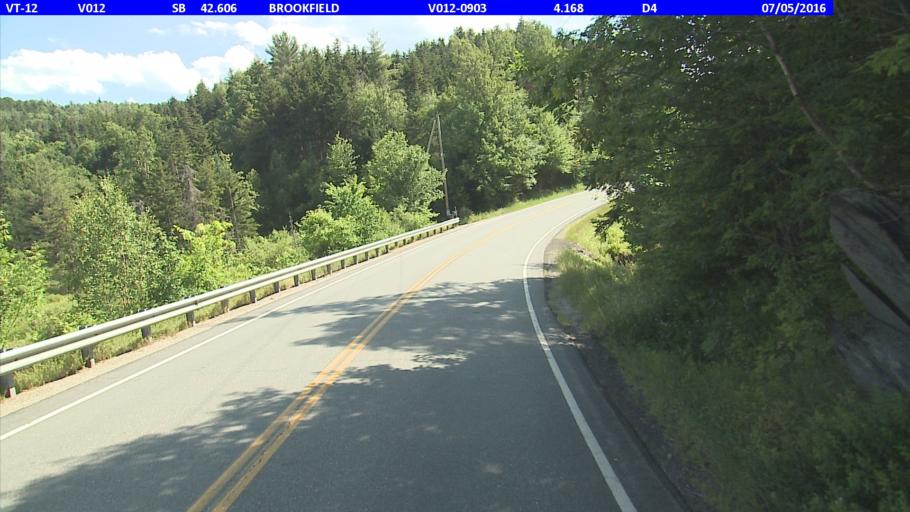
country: US
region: Vermont
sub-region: Washington County
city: Northfield
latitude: 44.0603
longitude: -72.6350
